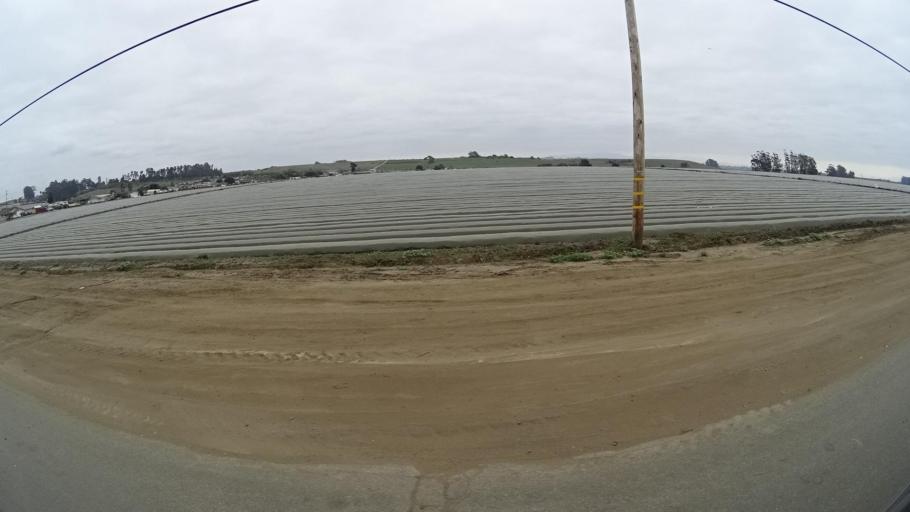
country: US
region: California
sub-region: Monterey County
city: Elkhorn
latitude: 36.8293
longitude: -121.7807
